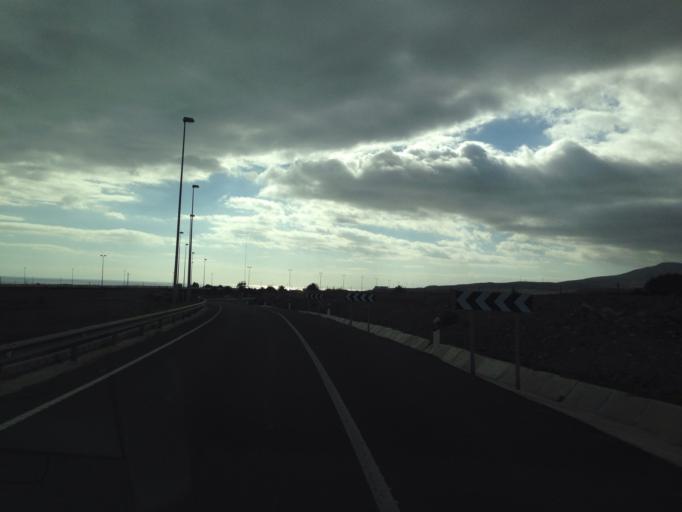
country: ES
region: Canary Islands
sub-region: Provincia de Las Palmas
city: Cruce de Arinaga
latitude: 27.8252
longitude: -15.4578
